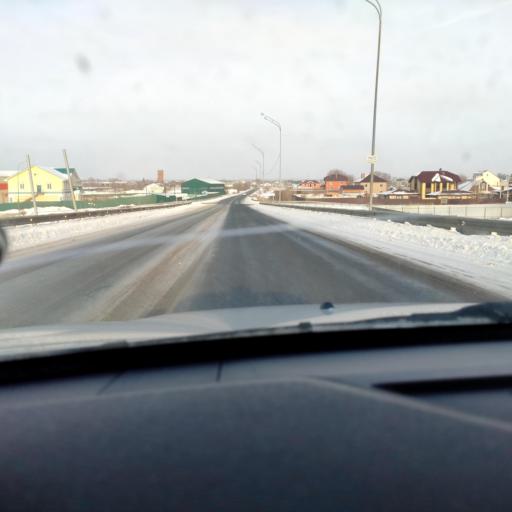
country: RU
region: Samara
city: Smyshlyayevka
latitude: 53.1536
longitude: 50.3840
